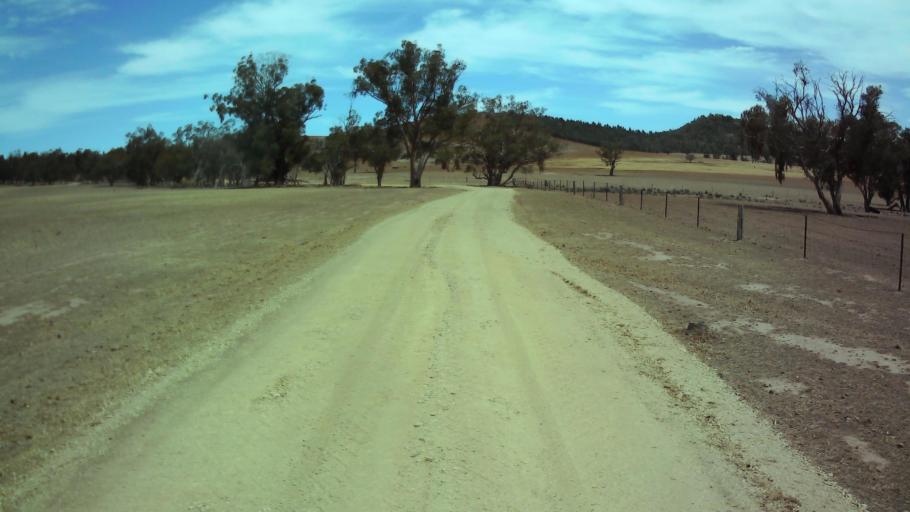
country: AU
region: New South Wales
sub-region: Weddin
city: Grenfell
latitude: -33.7827
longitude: 148.1515
